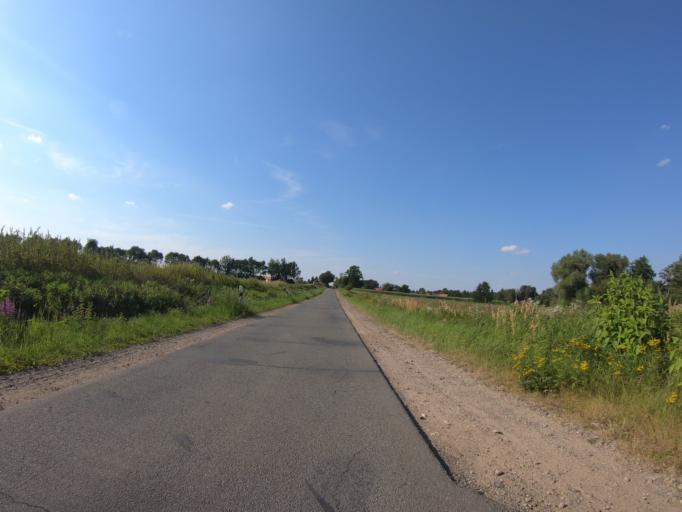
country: DE
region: Lower Saxony
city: Wieren
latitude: 52.8769
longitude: 10.6558
